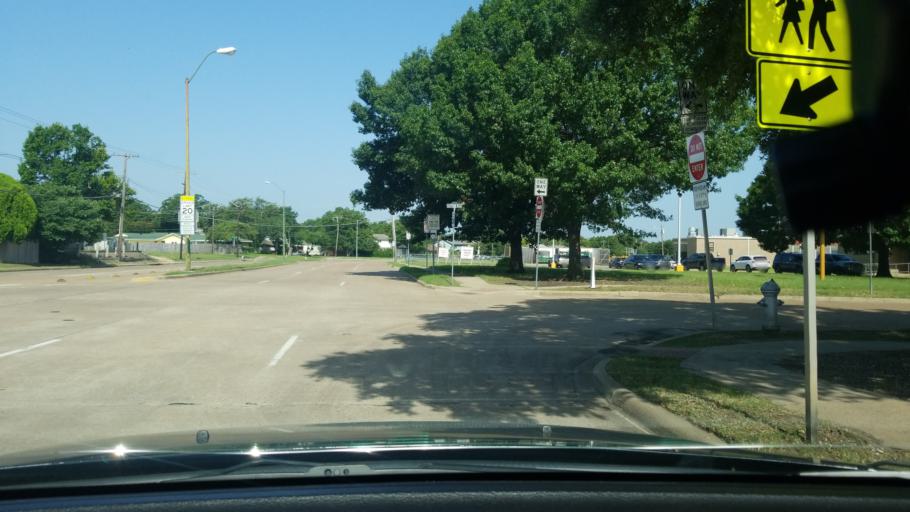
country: US
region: Texas
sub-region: Dallas County
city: Highland Park
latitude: 32.8072
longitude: -96.6937
